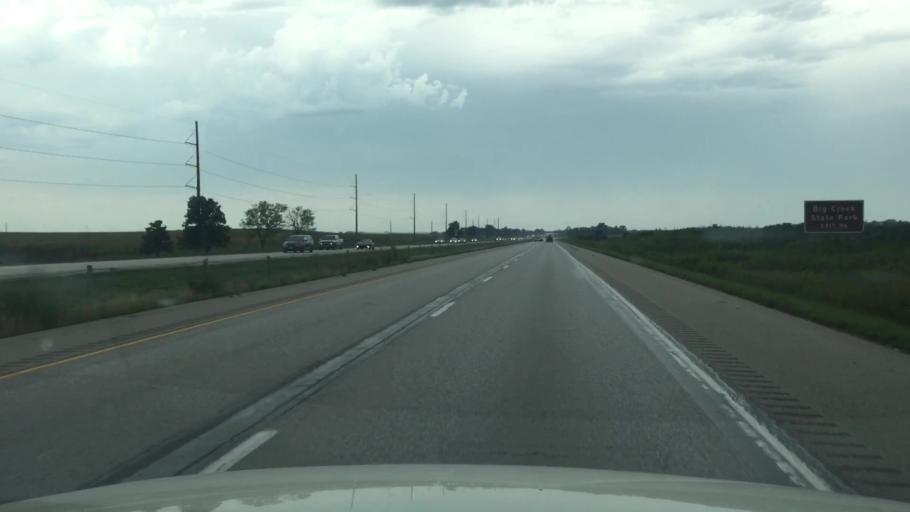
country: US
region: Iowa
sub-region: Polk County
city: Ankeny
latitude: 41.8039
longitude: -93.5708
